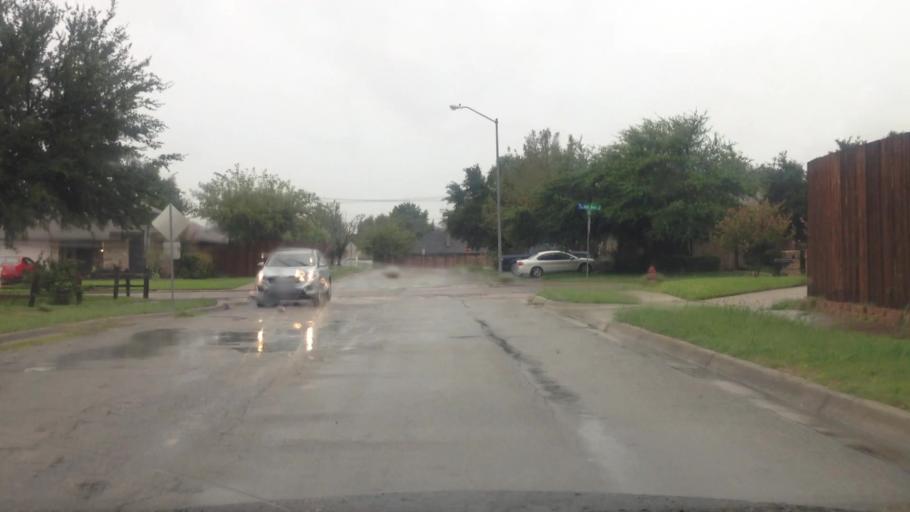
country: US
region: Texas
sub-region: Tarrant County
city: North Richland Hills
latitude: 32.8663
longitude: -97.2228
